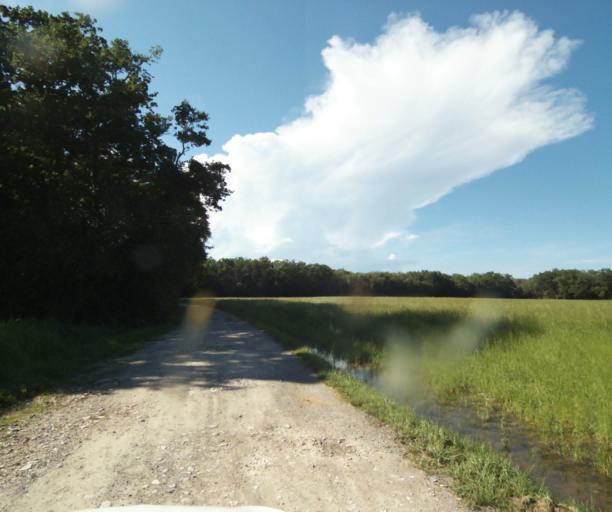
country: FR
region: Rhone-Alpes
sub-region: Departement de la Haute-Savoie
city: Messery
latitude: 46.3338
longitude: 6.2992
